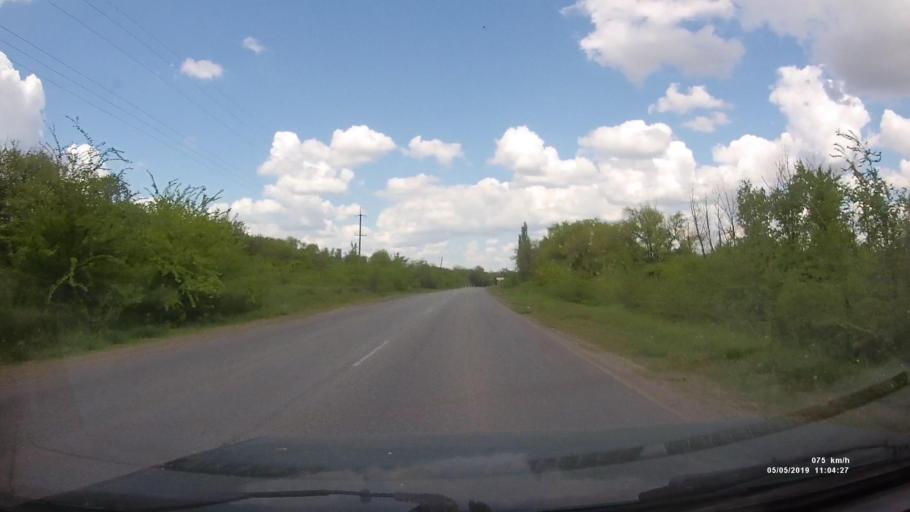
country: RU
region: Rostov
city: Ust'-Donetskiy
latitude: 47.6973
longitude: 40.9180
